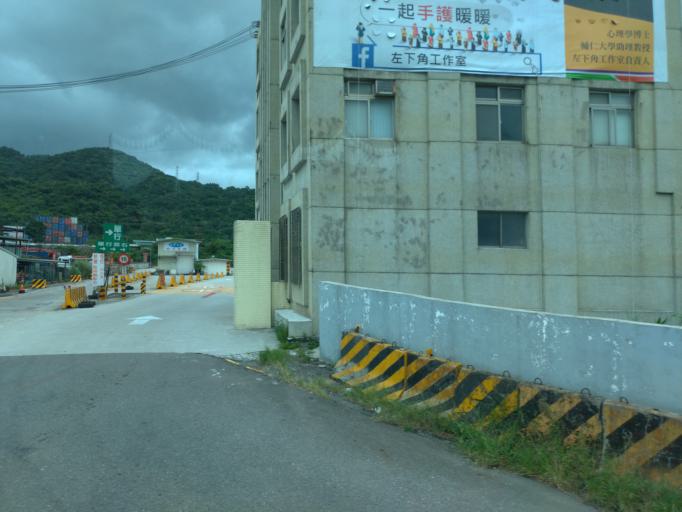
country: TW
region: Taiwan
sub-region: Keelung
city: Keelung
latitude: 25.0989
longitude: 121.7471
